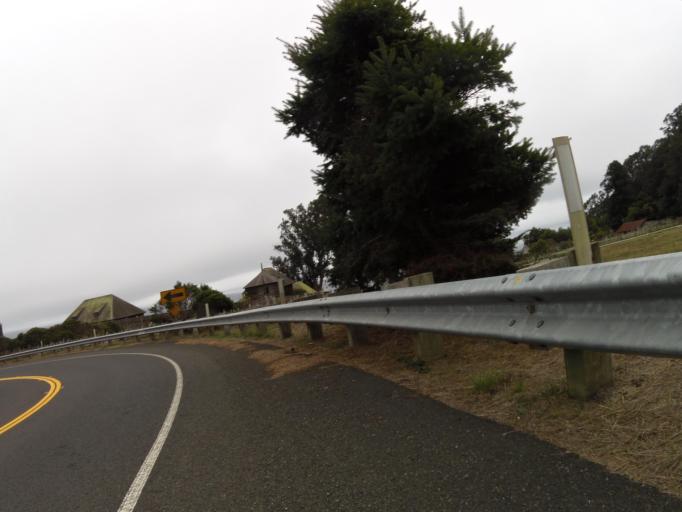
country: US
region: California
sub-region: Sonoma County
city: Monte Rio
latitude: 38.5156
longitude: -123.2436
